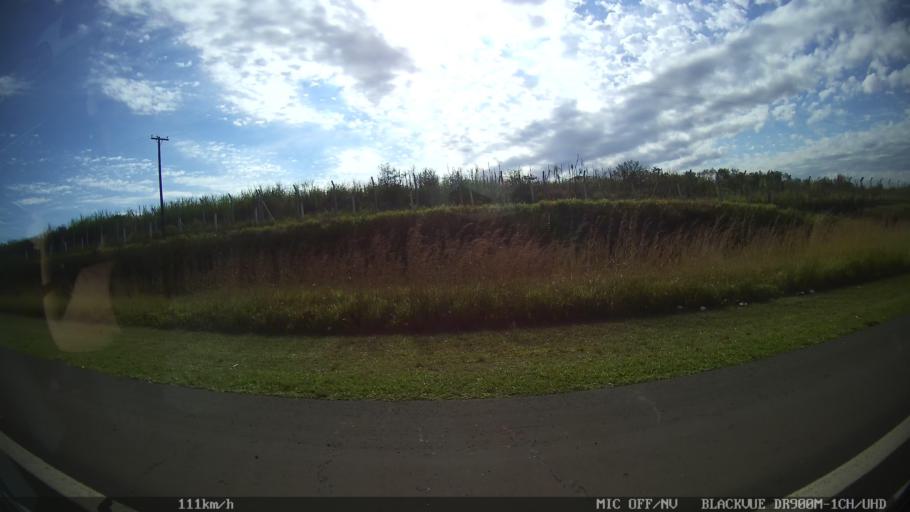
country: BR
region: Sao Paulo
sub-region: Iracemapolis
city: Iracemapolis
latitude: -22.6258
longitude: -47.4971
